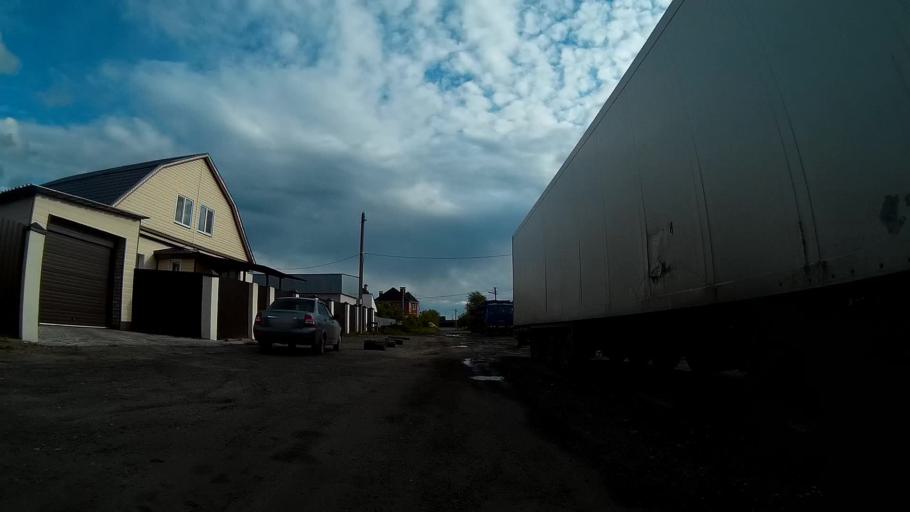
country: RU
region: Ulyanovsk
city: Novoul'yanovsk
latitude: 54.2012
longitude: 48.2730
